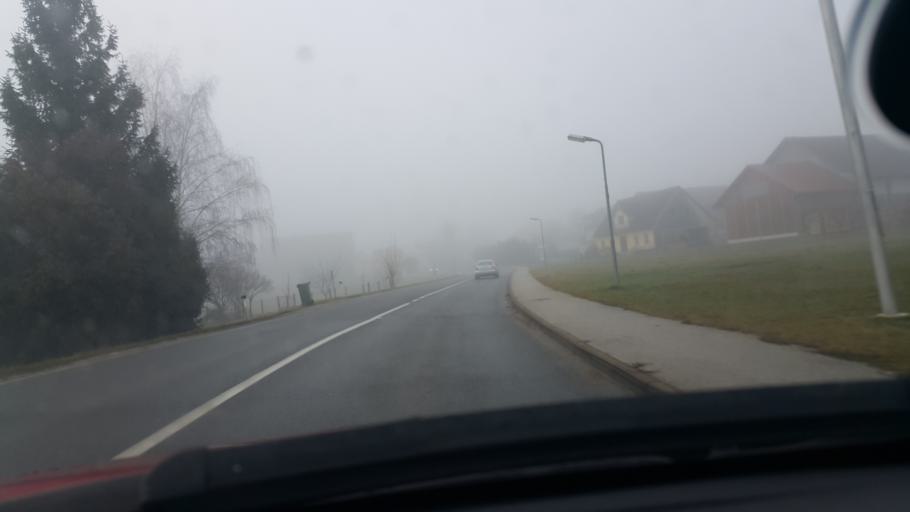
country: SI
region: Podcetrtek
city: Podcetrtek
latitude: 46.1340
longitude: 15.6005
